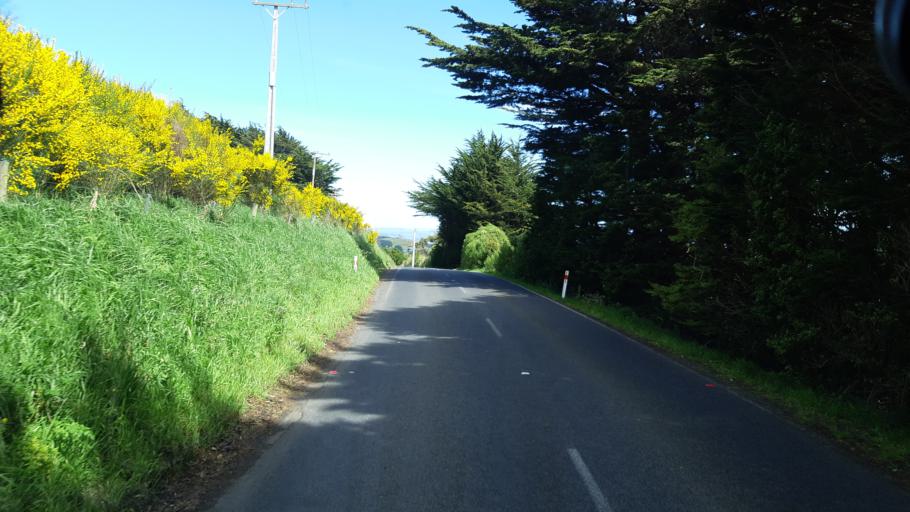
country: NZ
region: Otago
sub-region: Dunedin City
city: Portobello
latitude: -45.8812
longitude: 170.5953
